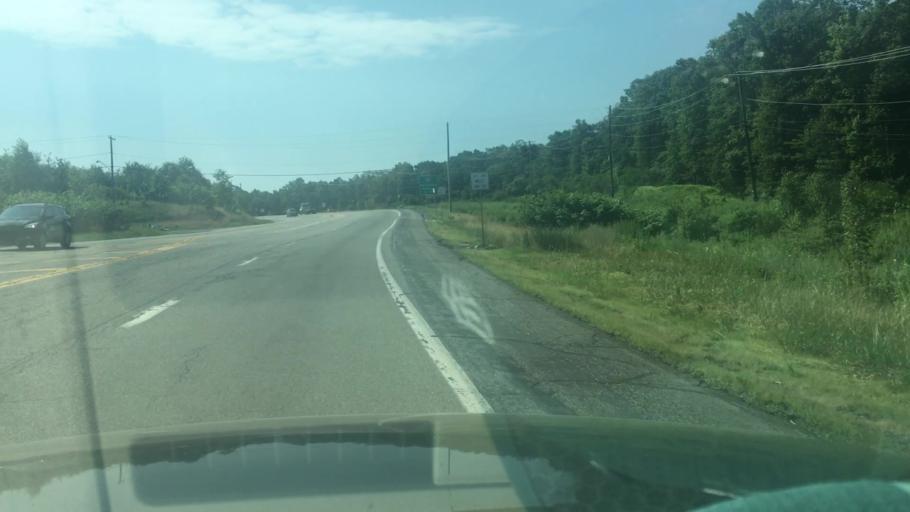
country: US
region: Pennsylvania
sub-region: Schuylkill County
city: Ashland
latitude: 40.7213
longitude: -76.3504
